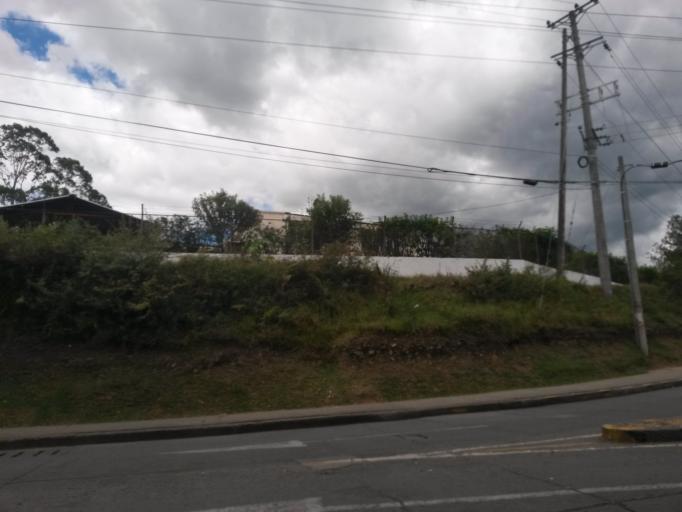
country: CO
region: Cauca
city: Popayan
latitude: 2.4516
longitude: -76.6320
